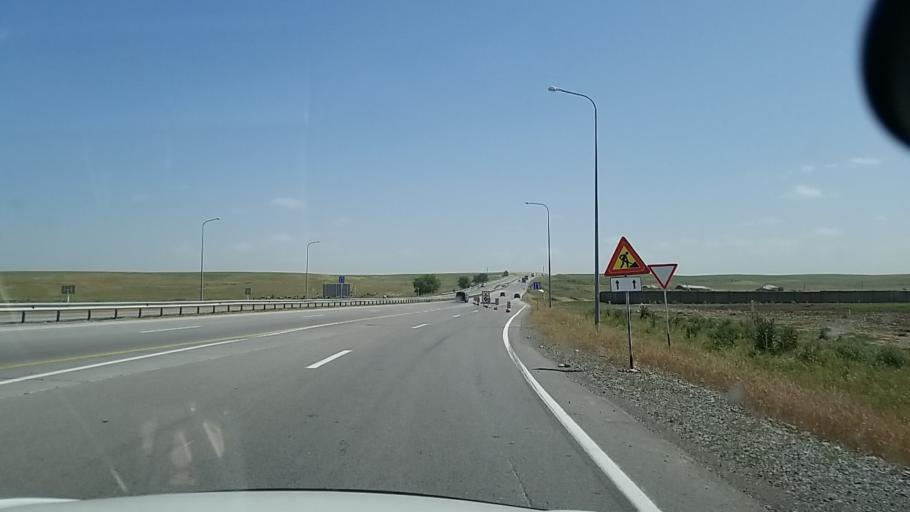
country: KZ
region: Ongtustik Qazaqstan
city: Aksu
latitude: 42.4404
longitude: 69.7247
